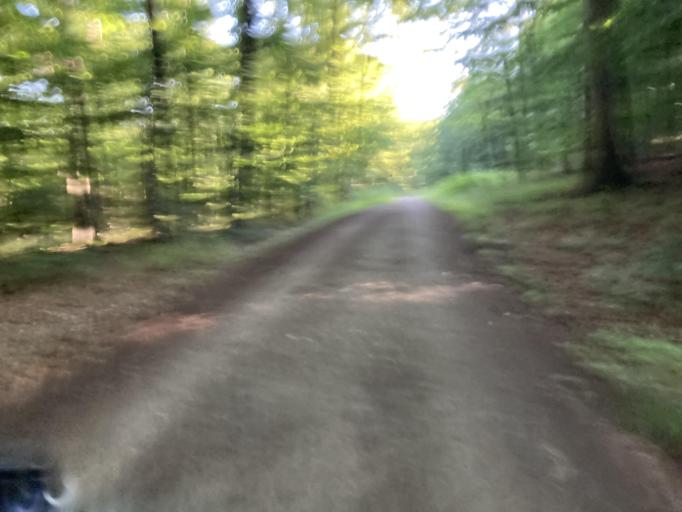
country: DE
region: Baden-Wuerttemberg
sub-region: Regierungsbezirk Stuttgart
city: Renningen
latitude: 48.7808
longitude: 8.9615
